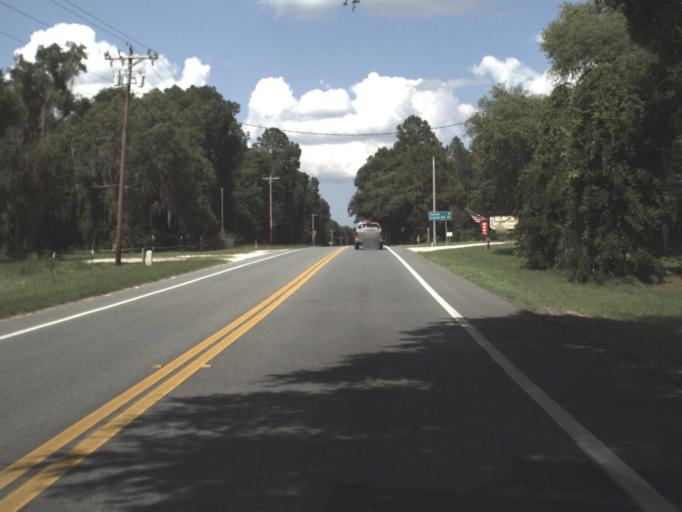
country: US
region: Florida
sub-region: Putnam County
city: Interlachen
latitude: 29.7288
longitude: -81.9157
